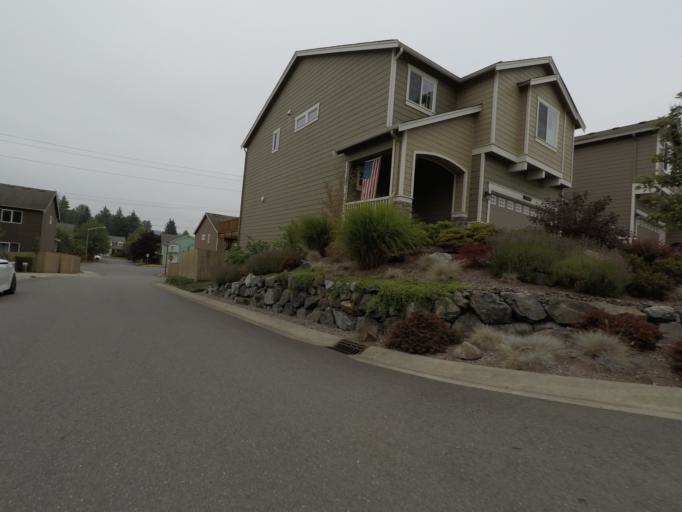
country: US
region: Washington
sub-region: King County
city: Kenmore
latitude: 47.7703
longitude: -122.2364
